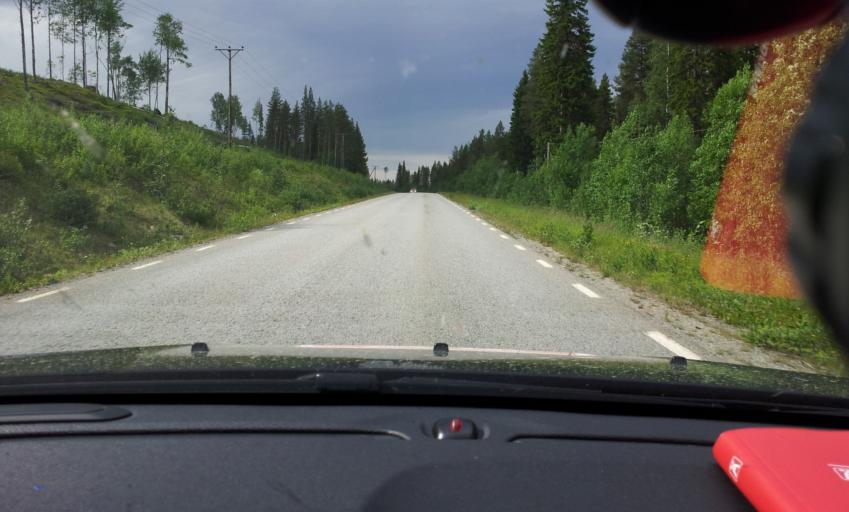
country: SE
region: Jaemtland
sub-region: Bergs Kommun
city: Hoverberg
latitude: 62.6655
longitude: 14.7301
